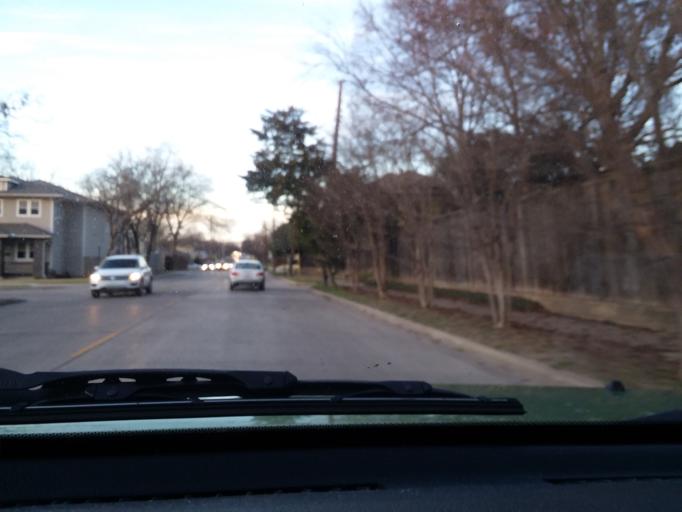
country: US
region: Texas
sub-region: Dallas County
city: Highland Park
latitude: 32.8189
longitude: -96.7702
